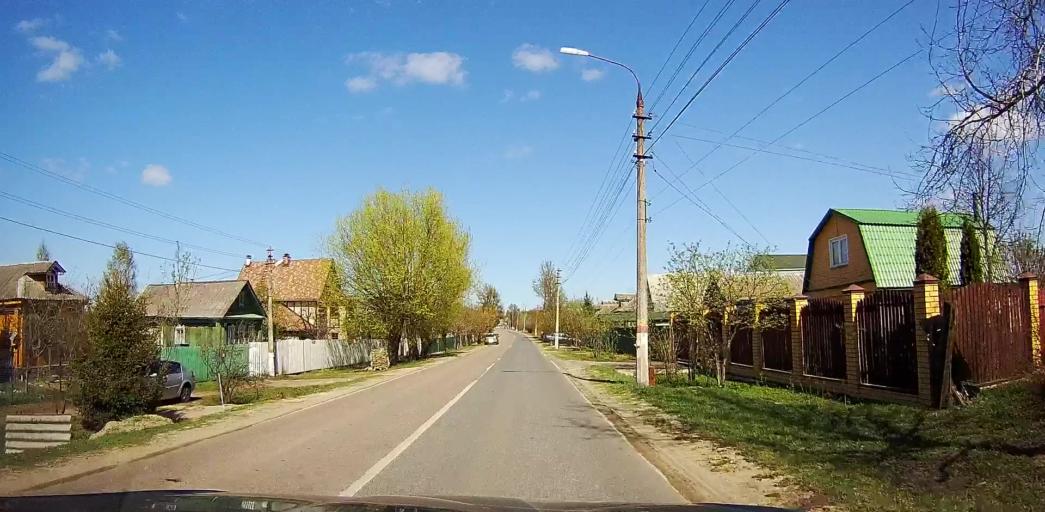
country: RU
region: Moskovskaya
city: Ramenskoye
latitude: 55.6190
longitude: 38.3028
